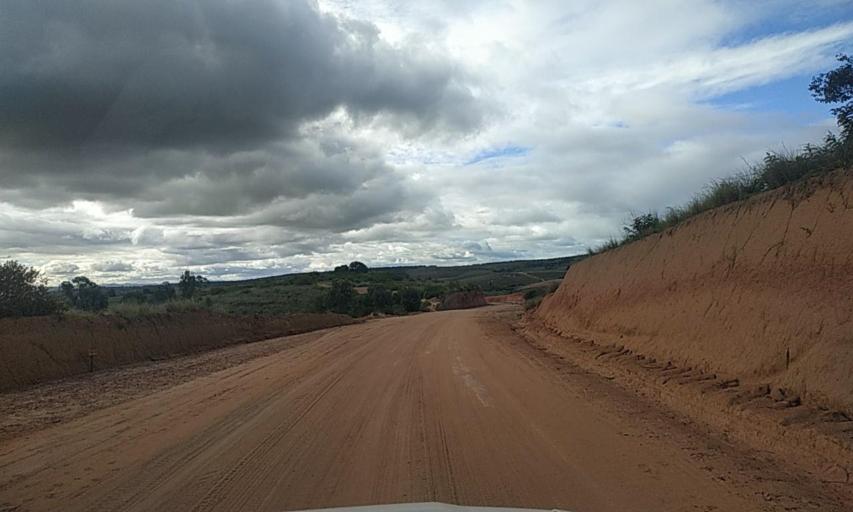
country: MG
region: Alaotra Mangoro
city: Ambatondrazaka
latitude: -17.9700
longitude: 48.2551
